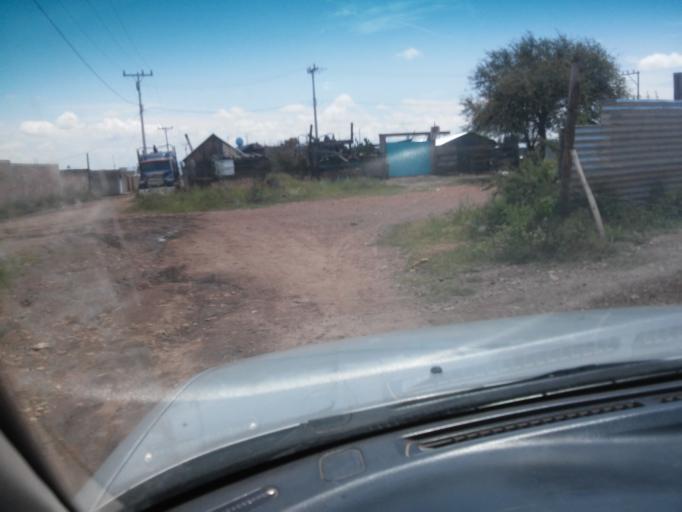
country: MX
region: Durango
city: Victoria de Durango
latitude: 23.9839
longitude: -104.7062
